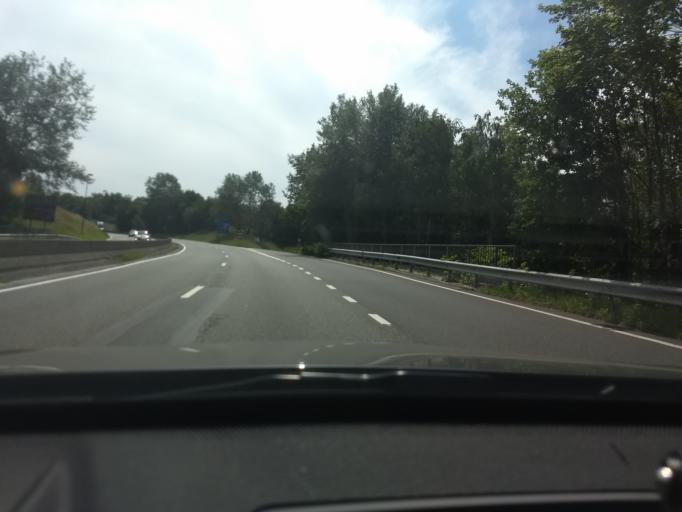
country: BE
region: Wallonia
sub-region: Province du Brabant Wallon
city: Louvain-la-Neuve
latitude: 50.6618
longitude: 4.6044
